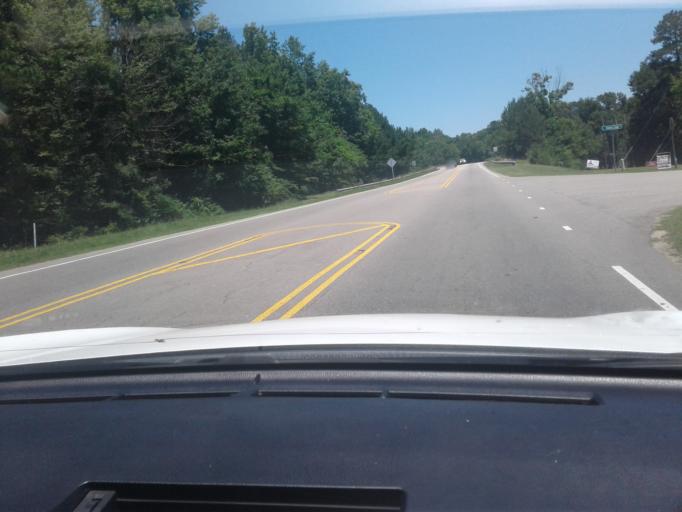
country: US
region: North Carolina
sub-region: Harnett County
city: Erwin
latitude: 35.3117
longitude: -78.6954
